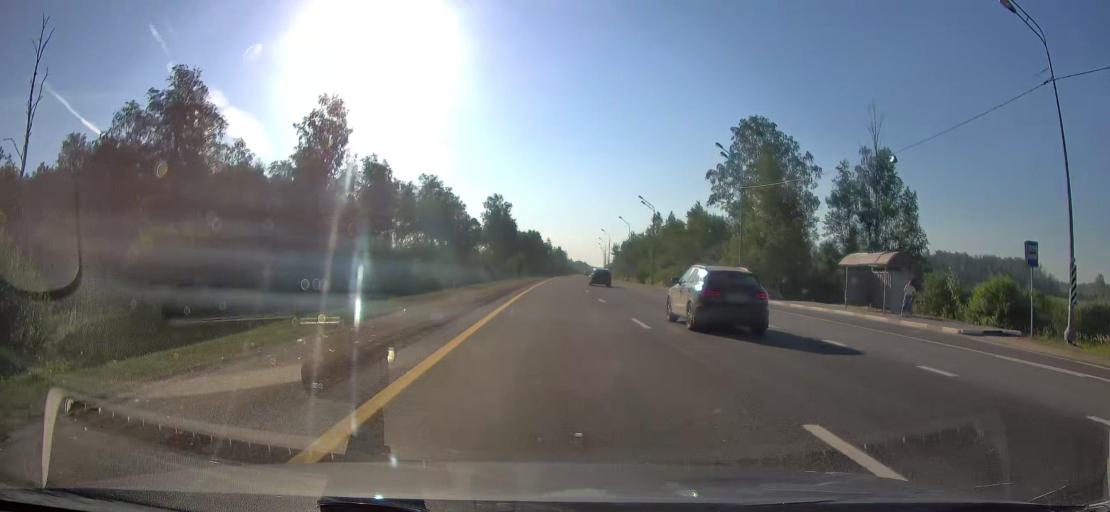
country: RU
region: Leningrad
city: Sinyavino
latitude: 59.9080
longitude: 31.0447
